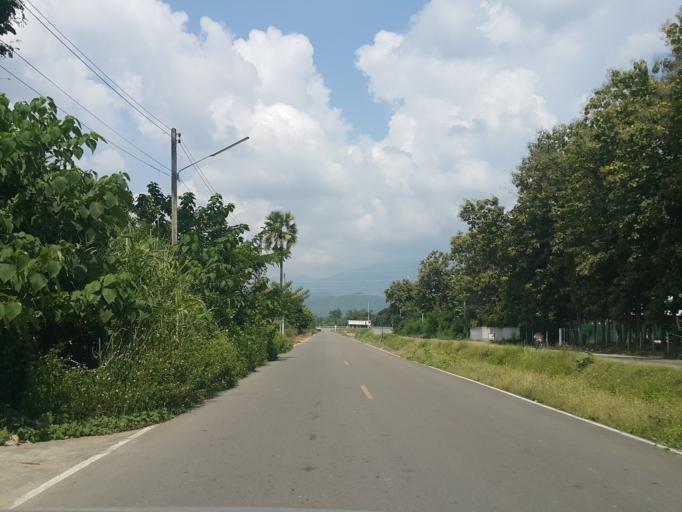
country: TH
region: Chiang Mai
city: Hang Dong
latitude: 18.7047
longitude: 98.9133
